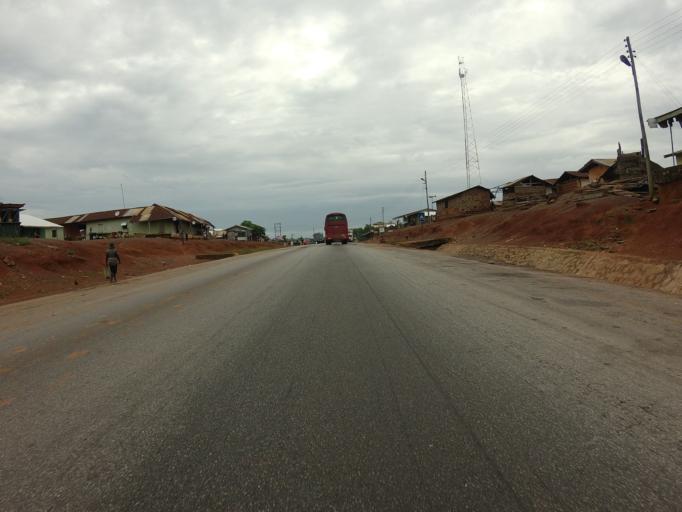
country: GH
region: Ashanti
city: Agogo
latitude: 6.6005
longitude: -0.9852
